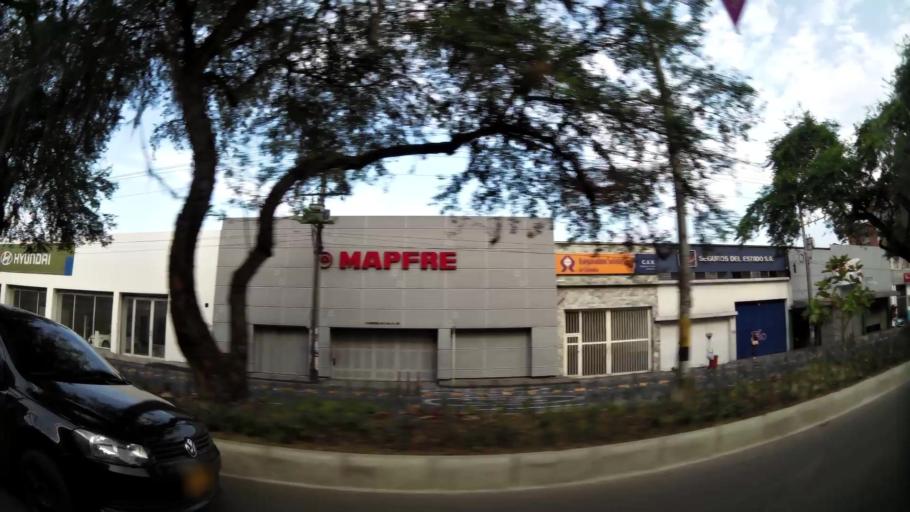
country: CO
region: Antioquia
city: Medellin
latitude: 6.2319
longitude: -75.5699
